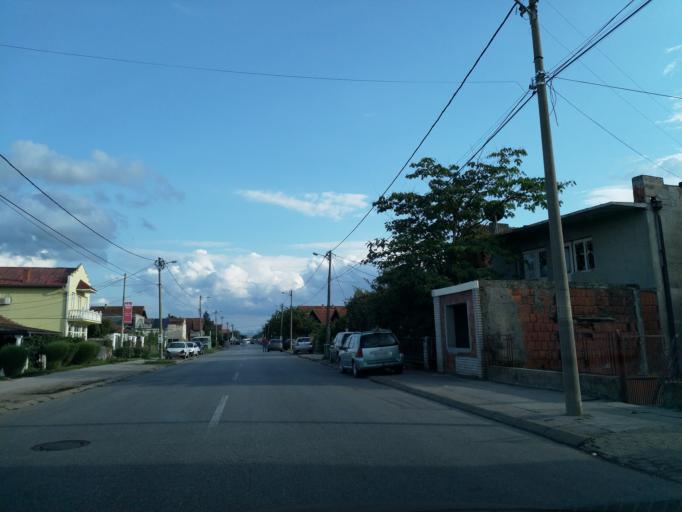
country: RS
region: Central Serbia
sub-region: Pomoravski Okrug
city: Paracin
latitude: 43.8505
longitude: 21.4134
